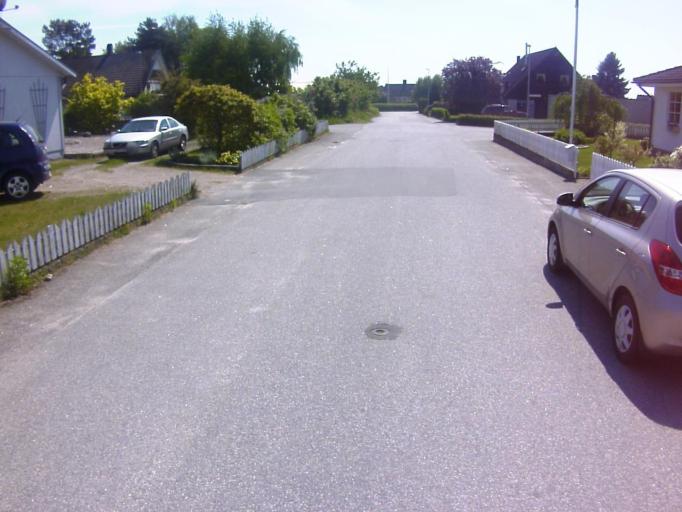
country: SE
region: Blekinge
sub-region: Solvesborgs Kommun
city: Soelvesborg
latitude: 56.0153
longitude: 14.6980
